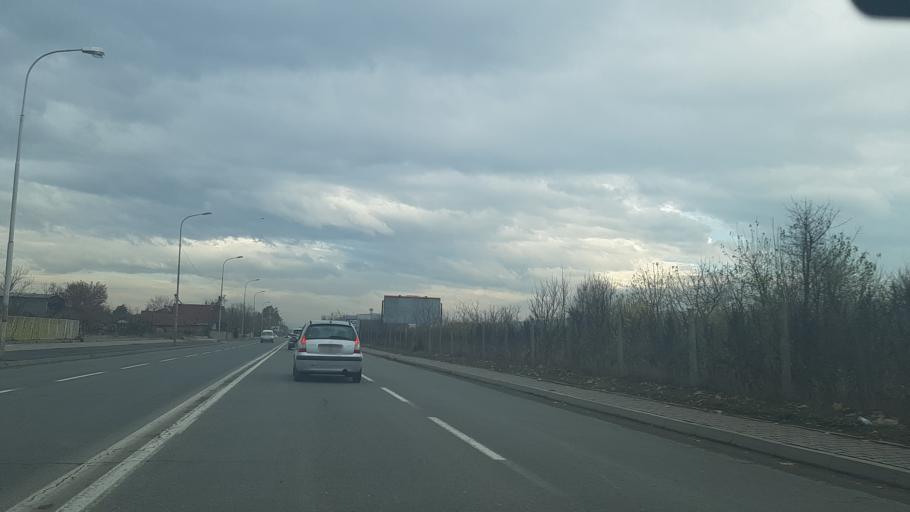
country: MK
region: Kisela Voda
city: Usje
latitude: 41.9778
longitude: 21.4480
